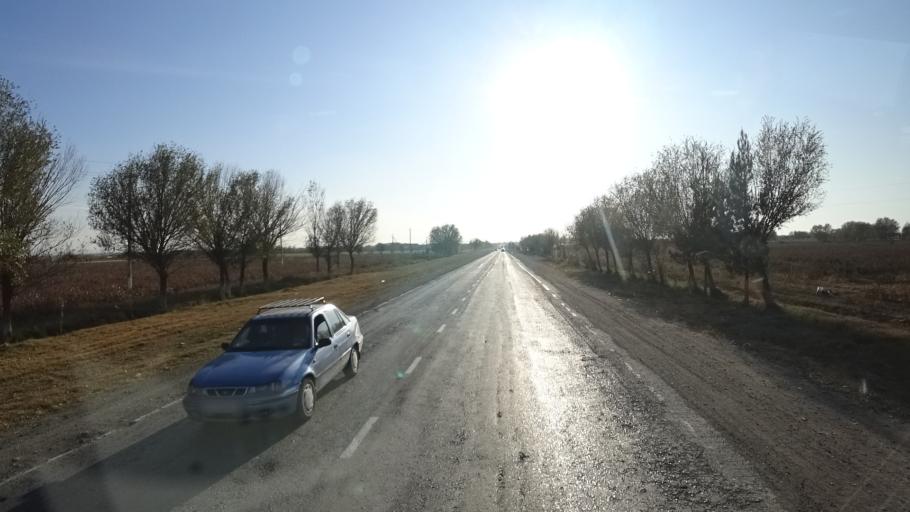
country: UZ
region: Navoiy
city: Beshrabot
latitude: 40.1803
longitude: 65.3502
